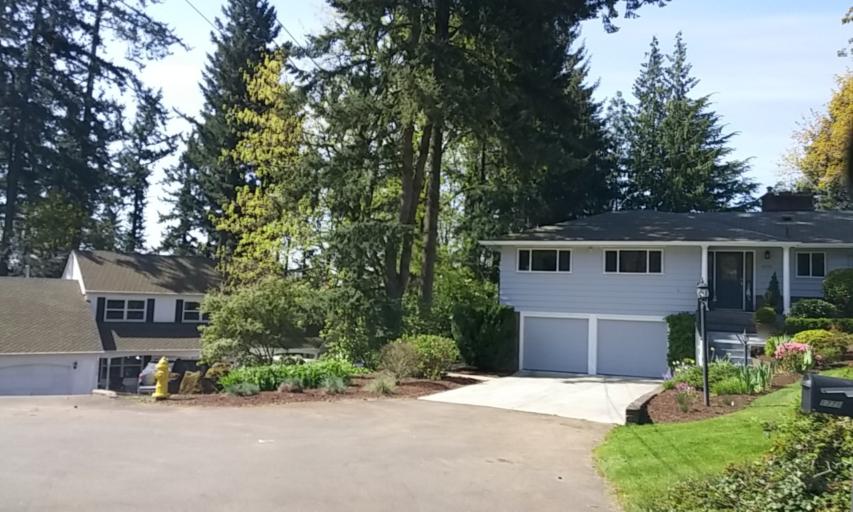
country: US
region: Oregon
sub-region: Washington County
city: West Slope
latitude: 45.5072
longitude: -122.7663
